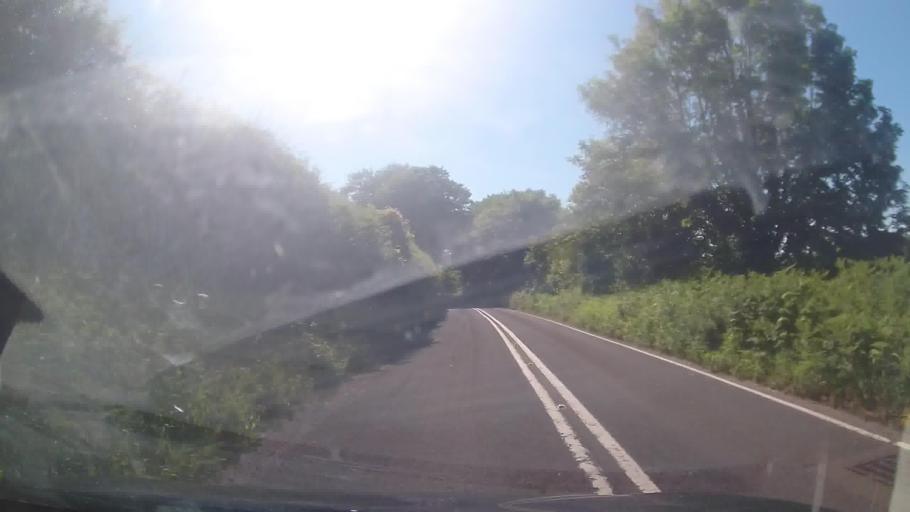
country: GB
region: England
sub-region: Devon
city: Dartmouth
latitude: 50.3705
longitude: -3.5516
